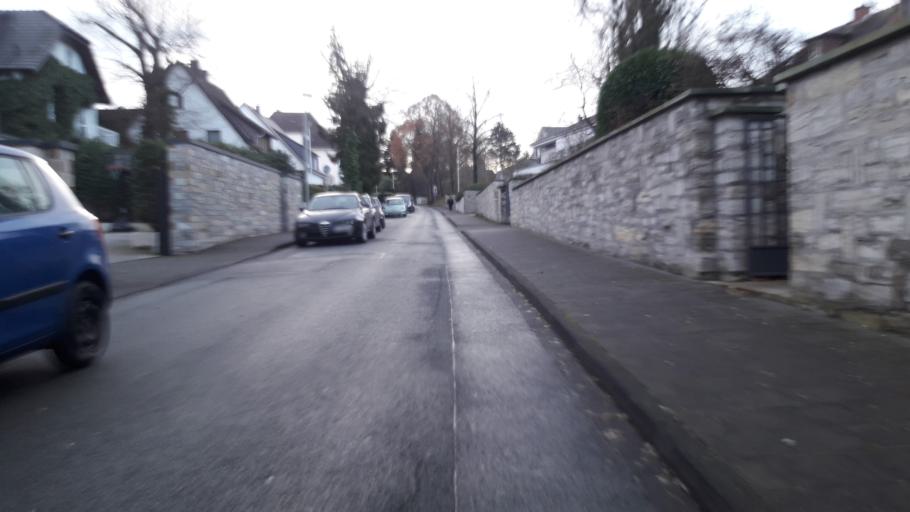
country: DE
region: North Rhine-Westphalia
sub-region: Regierungsbezirk Detmold
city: Paderborn
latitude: 51.7132
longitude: 8.7622
